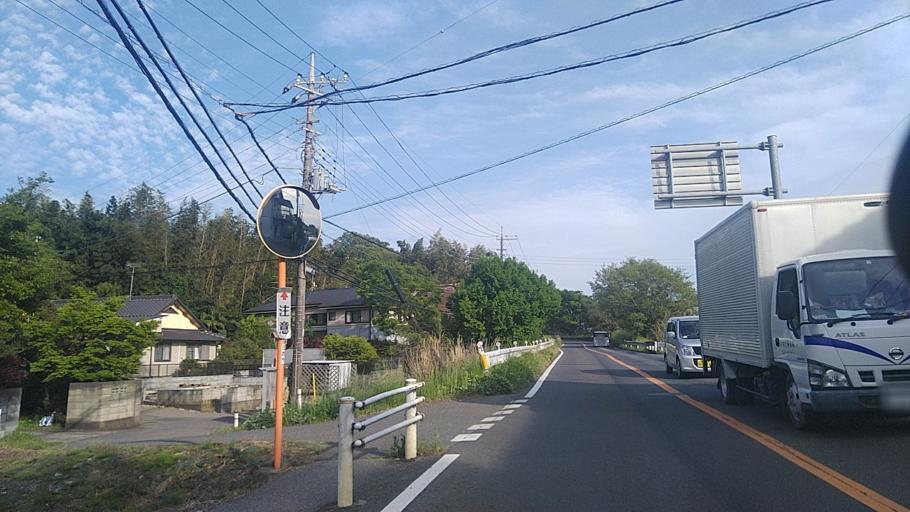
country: JP
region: Chiba
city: Shiroi
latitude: 35.7813
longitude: 140.1205
